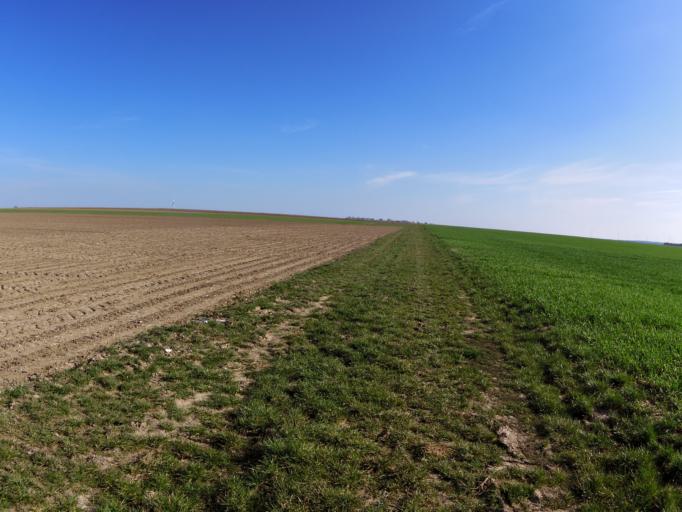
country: DE
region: Bavaria
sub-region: Regierungsbezirk Unterfranken
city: Prosselsheim
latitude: 49.8527
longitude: 10.1082
